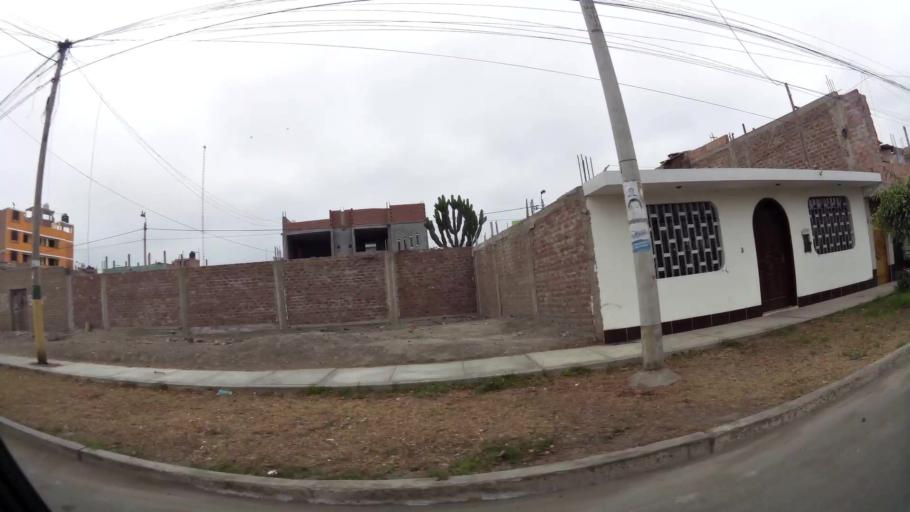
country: PE
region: Lima
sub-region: Barranca
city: Barranca
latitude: -10.7611
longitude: -77.7595
